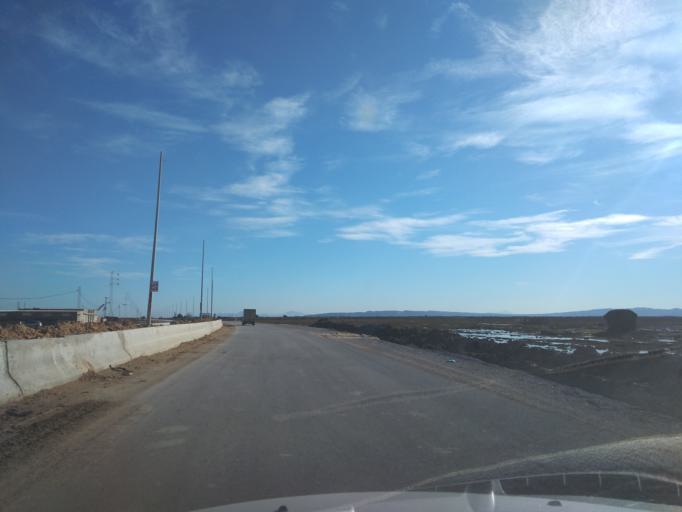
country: TN
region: Ariana
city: Qal'at al Andalus
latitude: 37.0480
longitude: 10.1245
